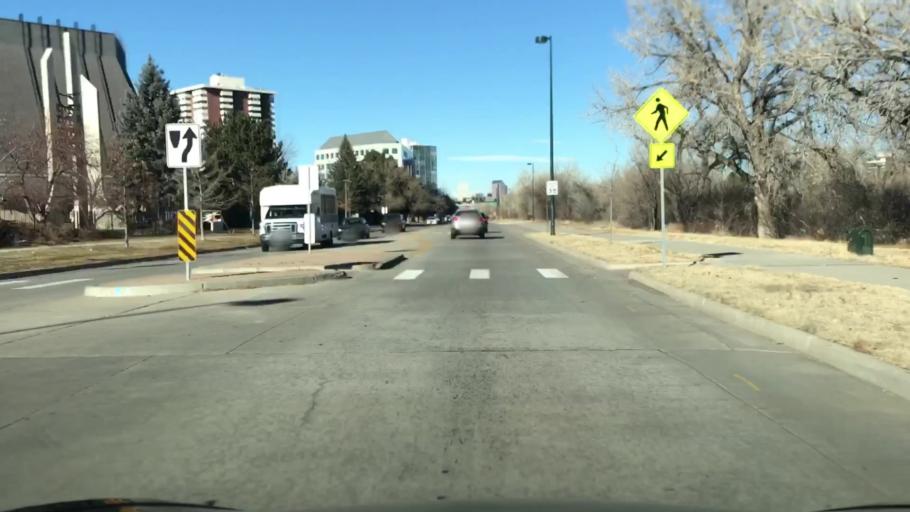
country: US
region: Colorado
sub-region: Arapahoe County
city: Glendale
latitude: 39.7095
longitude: -104.9462
